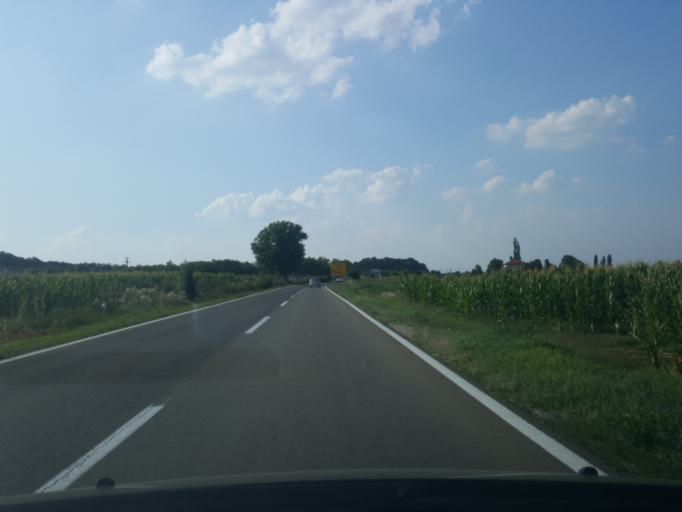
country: RS
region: Central Serbia
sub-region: Belgrade
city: Mladenovac
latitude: 44.3843
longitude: 20.6705
